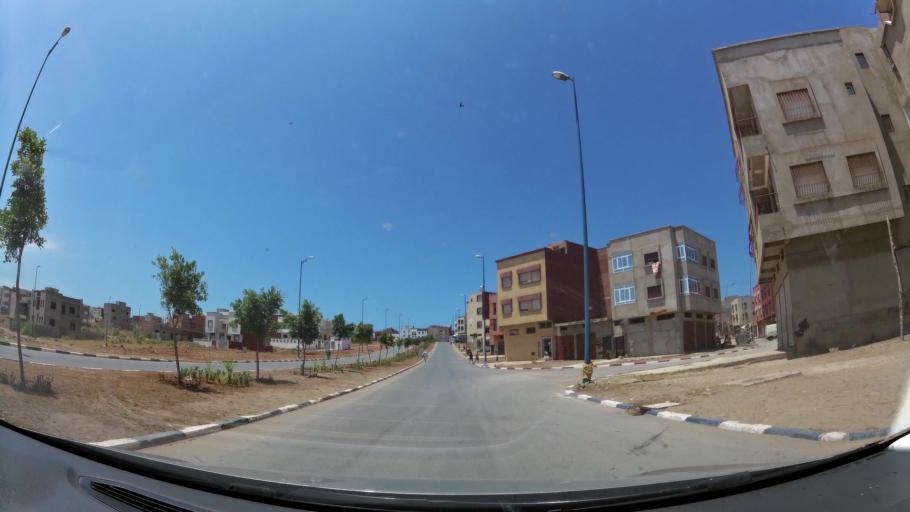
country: MA
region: Gharb-Chrarda-Beni Hssen
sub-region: Kenitra Province
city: Kenitra
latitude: 34.2570
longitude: -6.6524
